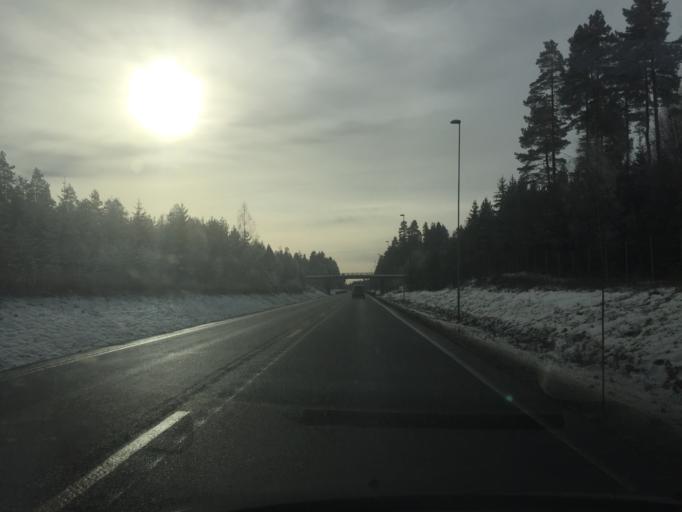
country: NO
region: Hedmark
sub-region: Loten
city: Loten
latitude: 60.7589
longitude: 11.3063
